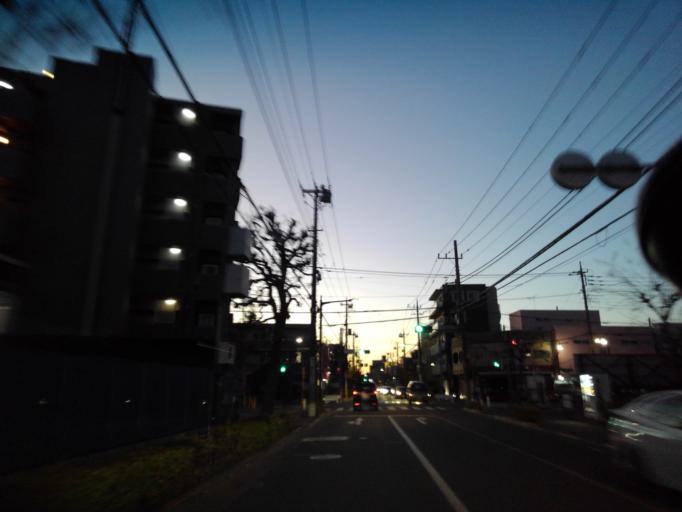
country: JP
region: Tokyo
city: Chofugaoka
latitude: 35.6465
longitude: 139.5510
